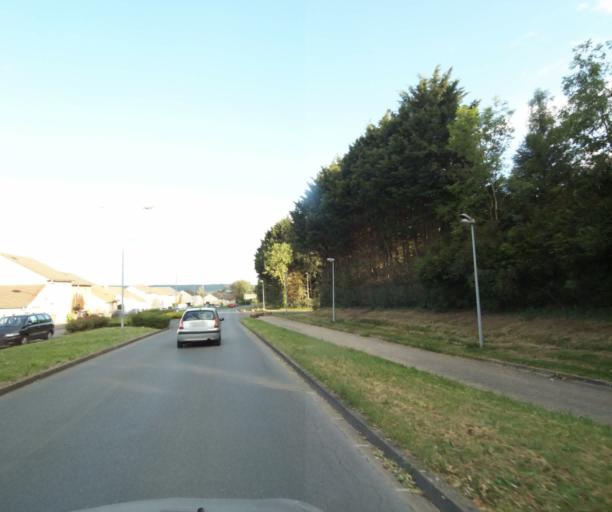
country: FR
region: Champagne-Ardenne
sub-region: Departement des Ardennes
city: Charleville-Mezieres
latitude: 49.7924
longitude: 4.7224
